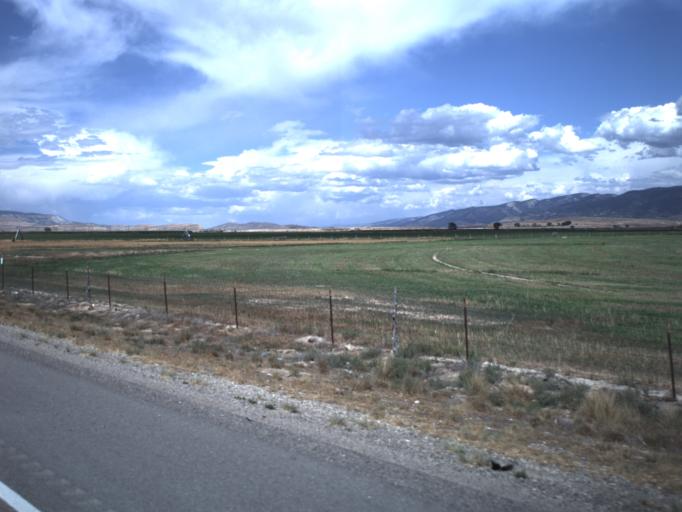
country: US
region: Utah
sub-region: Sanpete County
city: Centerfield
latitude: 39.0862
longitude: -111.8201
